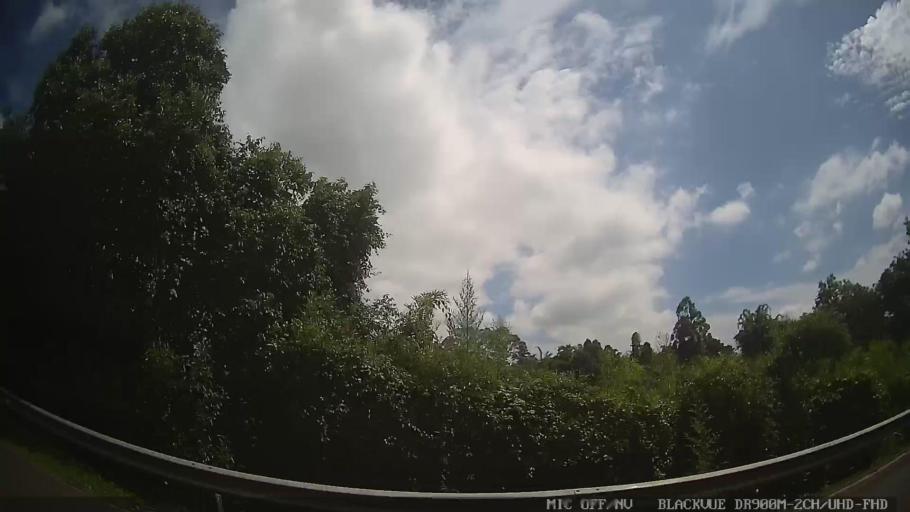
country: BR
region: Sao Paulo
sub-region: Tiete
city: Tiete
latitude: -23.1075
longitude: -47.7561
